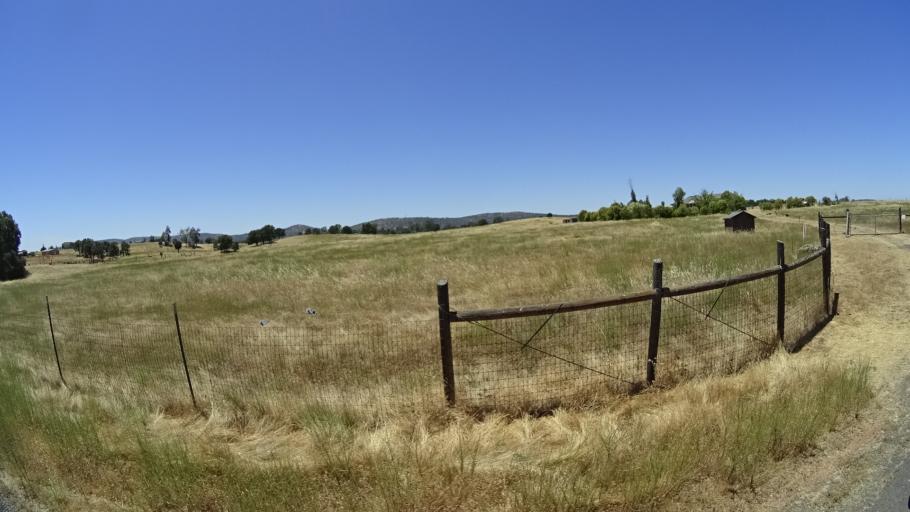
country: US
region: California
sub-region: Calaveras County
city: Copperopolis
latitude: 37.9820
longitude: -120.6670
